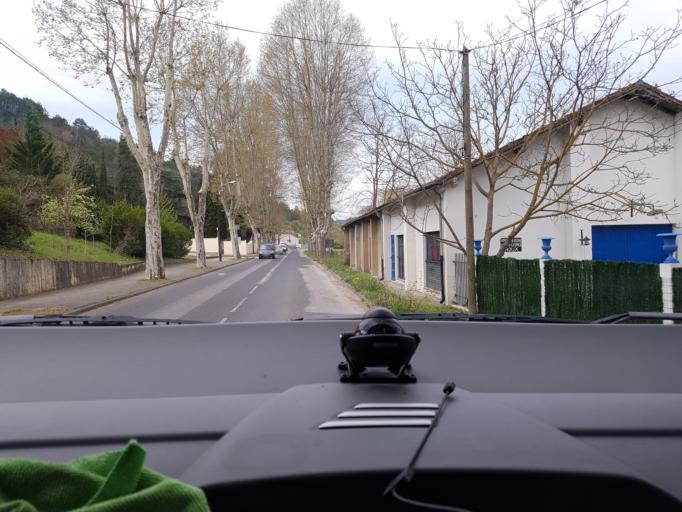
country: FR
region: Languedoc-Roussillon
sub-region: Departement de l'Aude
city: Couiza
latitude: 42.9396
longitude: 2.2472
